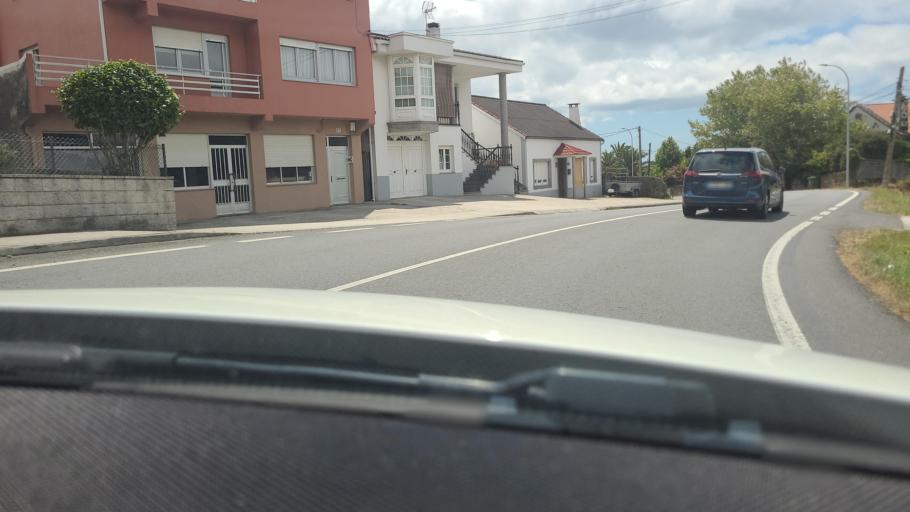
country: ES
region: Galicia
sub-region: Provincia da Coruna
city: Cee
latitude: 42.9474
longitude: -9.1795
